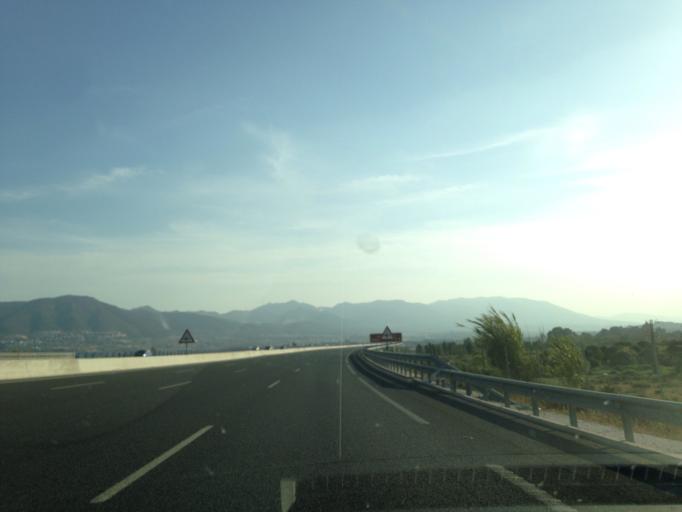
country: ES
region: Andalusia
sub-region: Provincia de Malaga
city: Alhaurin de la Torre
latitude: 36.6992
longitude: -4.5172
